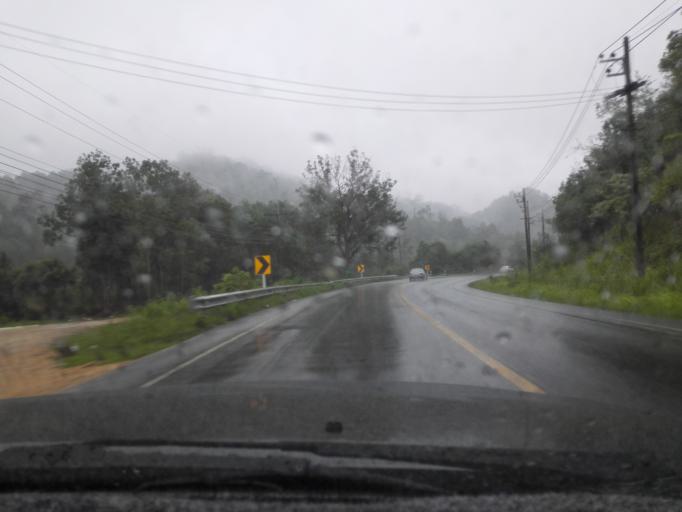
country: TH
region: Tak
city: Tak
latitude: 16.7884
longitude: 98.9452
